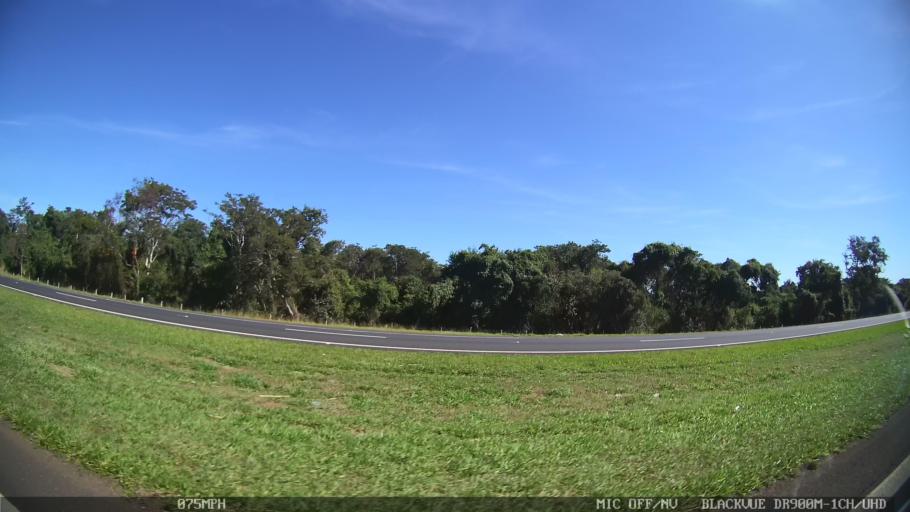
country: BR
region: Sao Paulo
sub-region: Santa Rita Do Passa Quatro
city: Santa Rita do Passa Quatro
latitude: -21.6391
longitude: -47.6122
